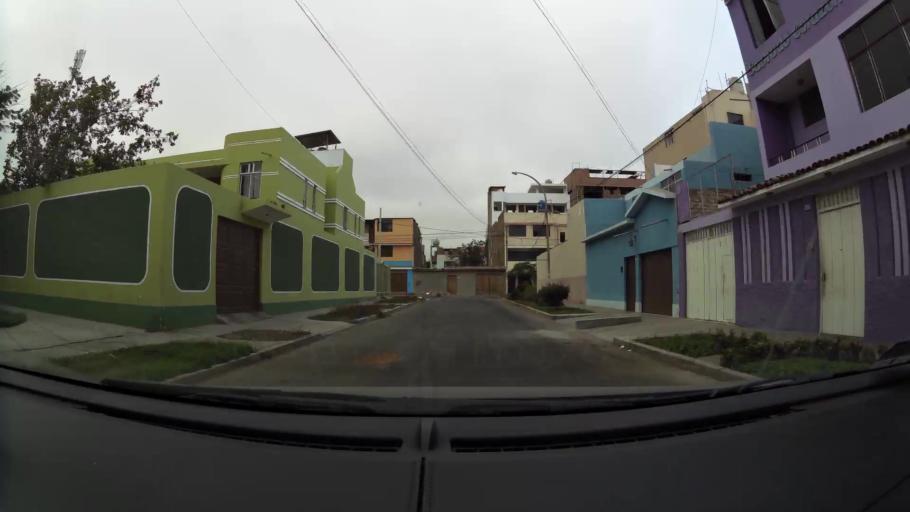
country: PE
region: La Libertad
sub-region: Provincia de Trujillo
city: Trujillo
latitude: -8.0992
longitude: -79.0295
